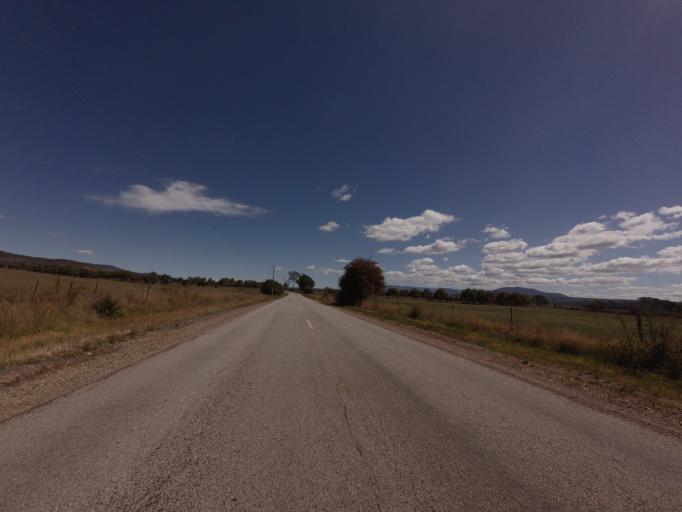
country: AU
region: Tasmania
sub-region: Break O'Day
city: St Helens
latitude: -41.6028
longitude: 148.0332
